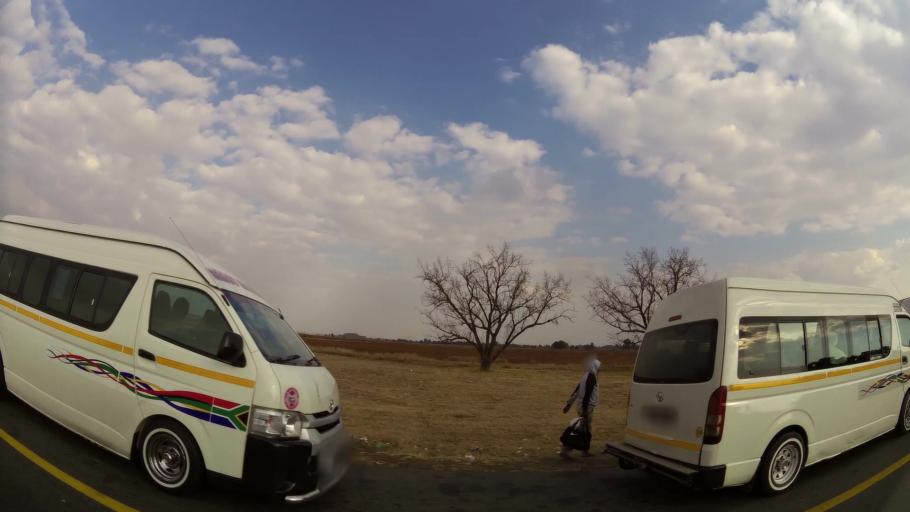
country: ZA
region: Gauteng
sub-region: Ekurhuleni Metropolitan Municipality
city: Springs
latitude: -26.2691
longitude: 28.4914
